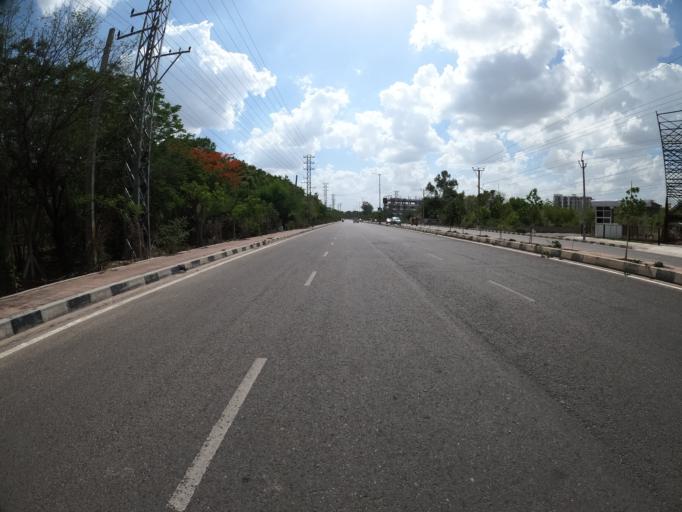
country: IN
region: Telangana
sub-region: Hyderabad
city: Hyderabad
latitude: 17.3507
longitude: 78.3689
